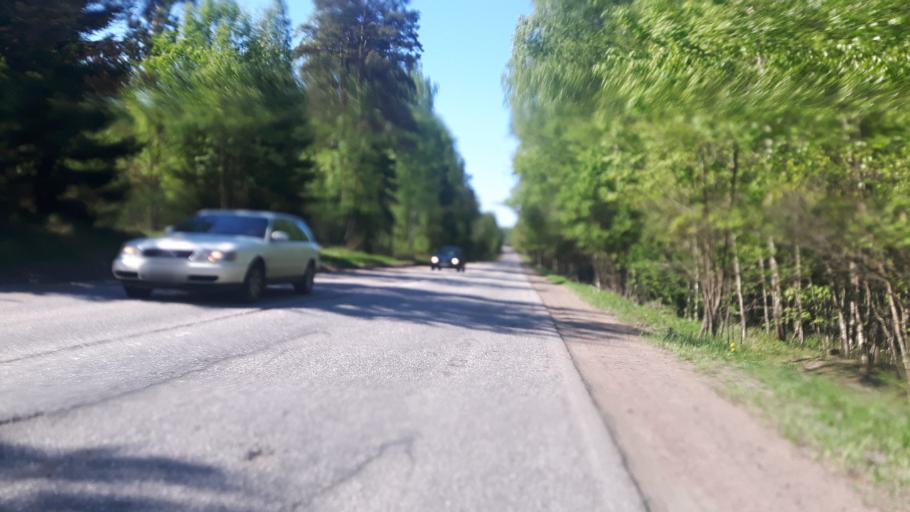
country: RU
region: Leningrad
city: Vyborg
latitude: 60.6450
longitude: 28.7452
